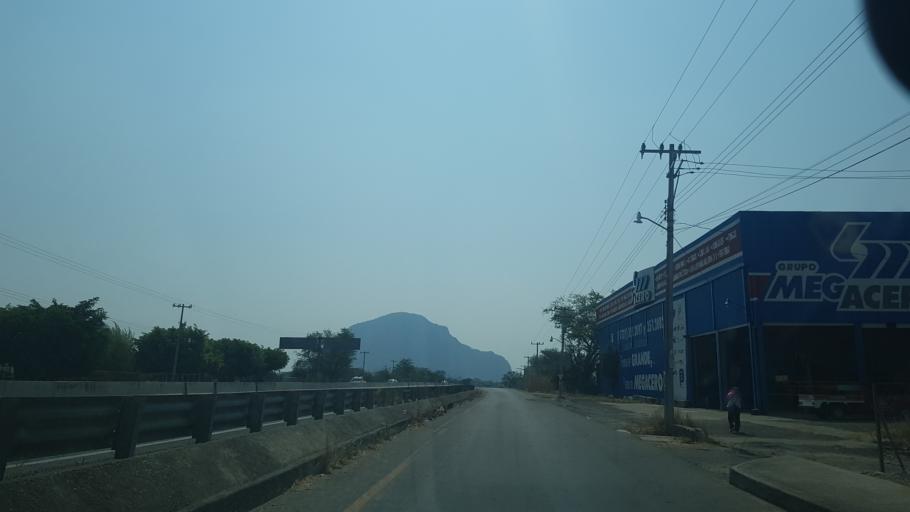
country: MX
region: Morelos
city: Amayuca
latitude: 18.7164
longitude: -98.7921
